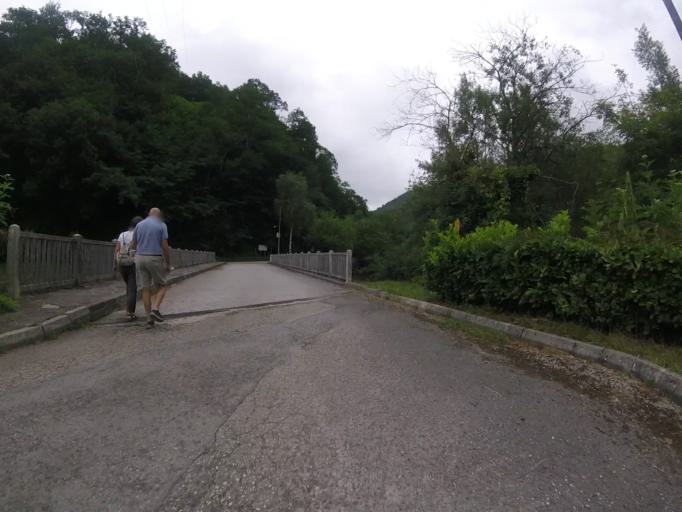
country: ES
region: Navarre
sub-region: Provincia de Navarra
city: Doneztebe
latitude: 43.1350
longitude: -1.6658
